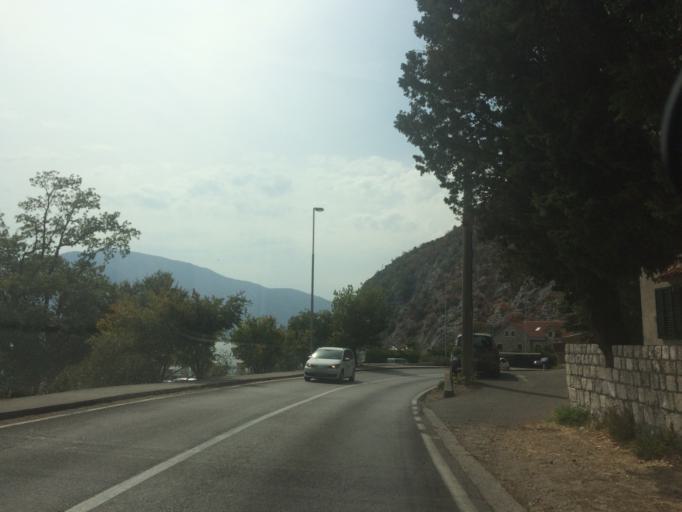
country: ME
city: Dobrota
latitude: 42.4901
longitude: 18.7561
